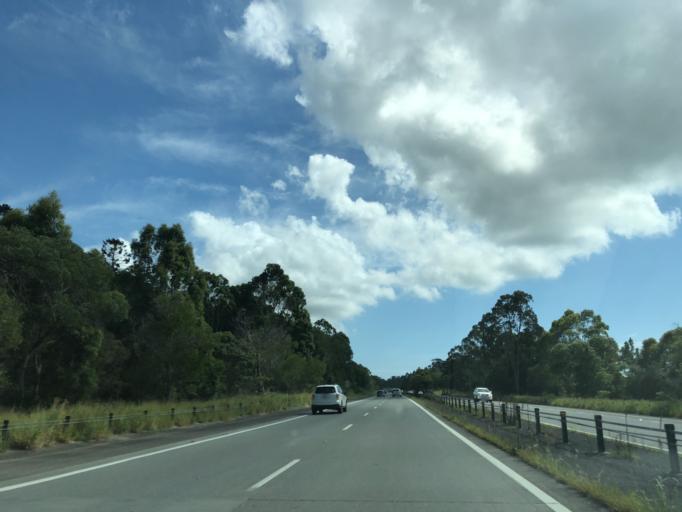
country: AU
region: New South Wales
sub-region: Tweed
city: Pottsville Beach
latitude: -28.4182
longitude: 153.5234
